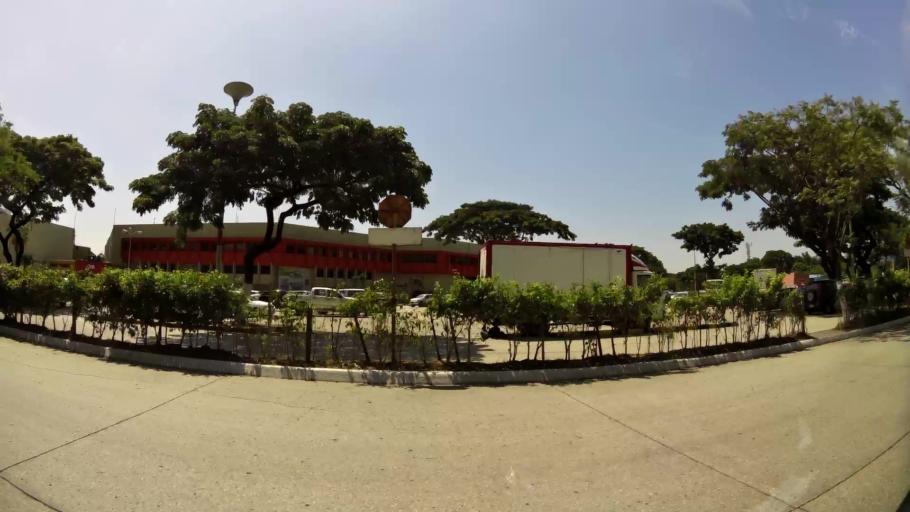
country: EC
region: Guayas
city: Guayaquil
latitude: -2.1699
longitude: -79.9173
